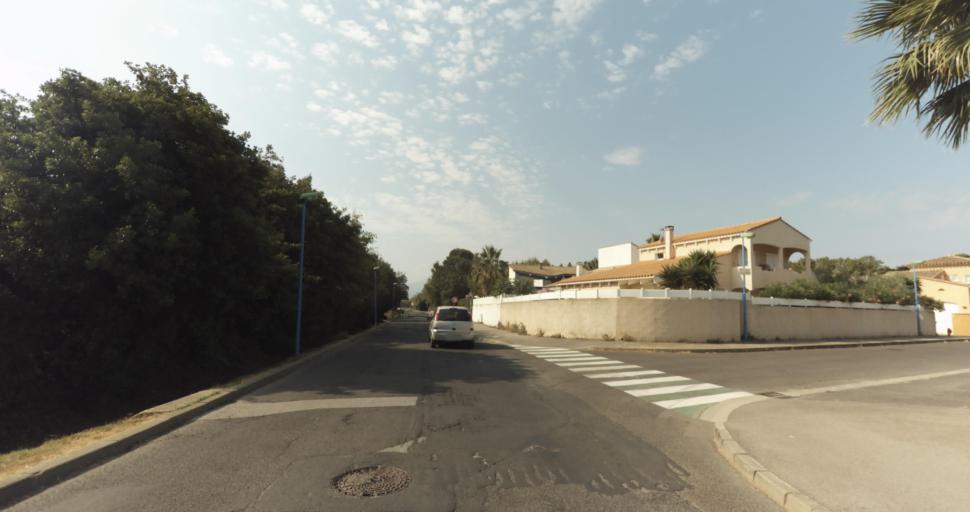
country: FR
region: Languedoc-Roussillon
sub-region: Departement des Pyrenees-Orientales
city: Saint-Cyprien-Plage
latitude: 42.6076
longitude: 3.0315
